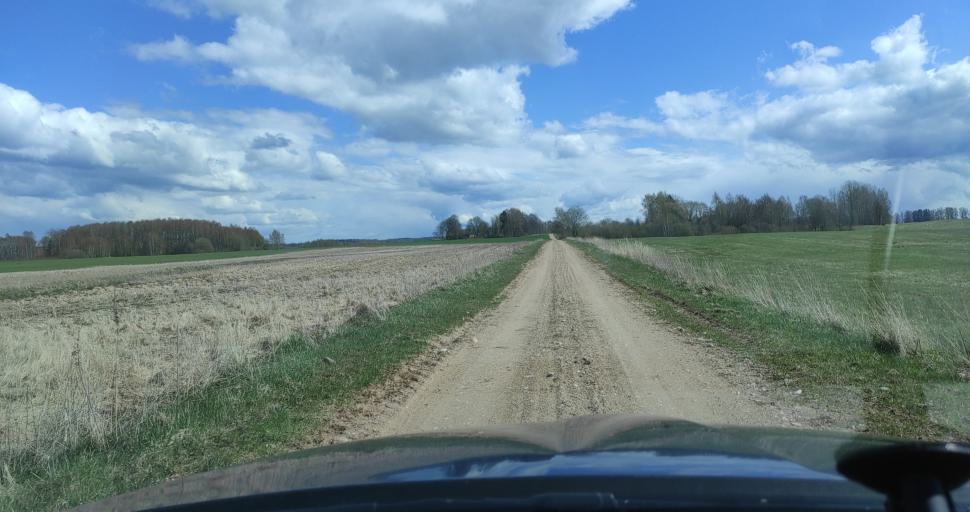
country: LV
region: Kuldigas Rajons
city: Kuldiga
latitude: 56.8703
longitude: 21.7908
